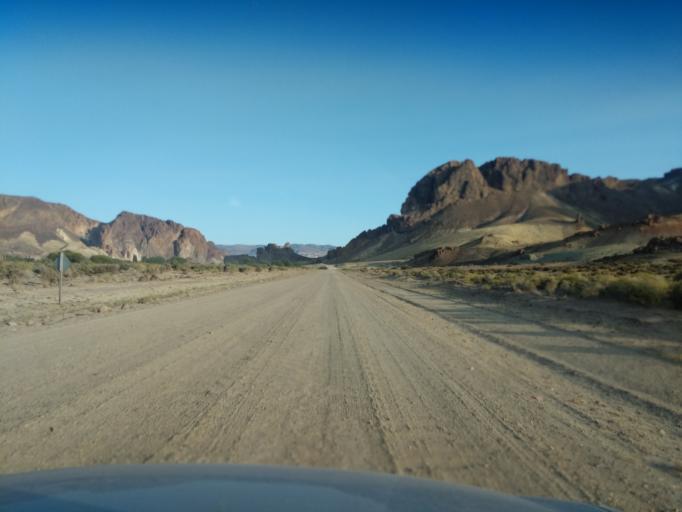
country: AR
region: Chubut
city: Leleque
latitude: -42.6556
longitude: -70.1319
